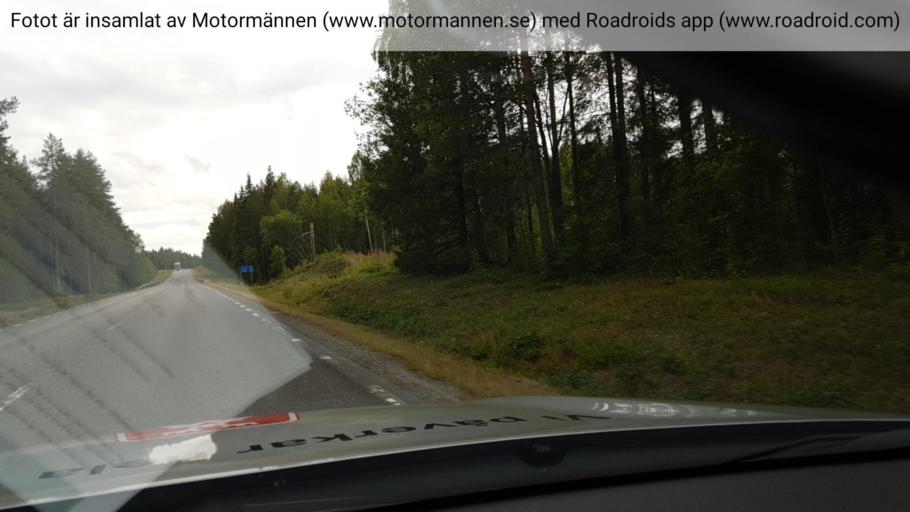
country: SE
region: Norrbotten
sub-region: Overkalix Kommun
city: OEverkalix
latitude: 66.2562
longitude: 22.8139
